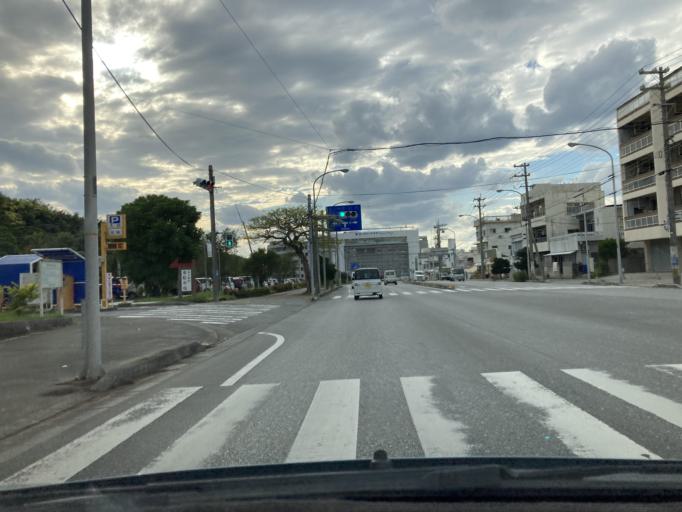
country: JP
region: Okinawa
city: Okinawa
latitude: 26.3638
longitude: 127.7598
